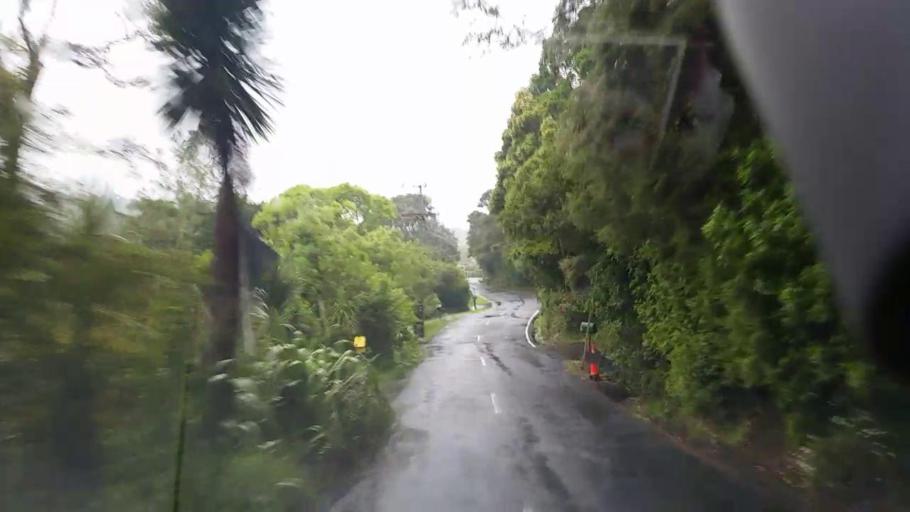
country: NZ
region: Auckland
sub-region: Auckland
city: Waitakere
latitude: -36.9033
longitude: 174.5741
